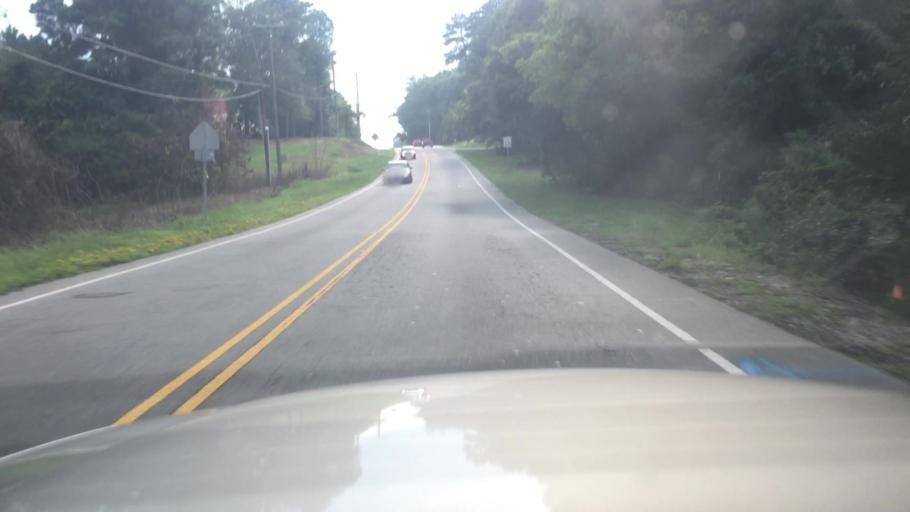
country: US
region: North Carolina
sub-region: Cumberland County
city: Fayetteville
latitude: 35.0613
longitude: -78.9439
